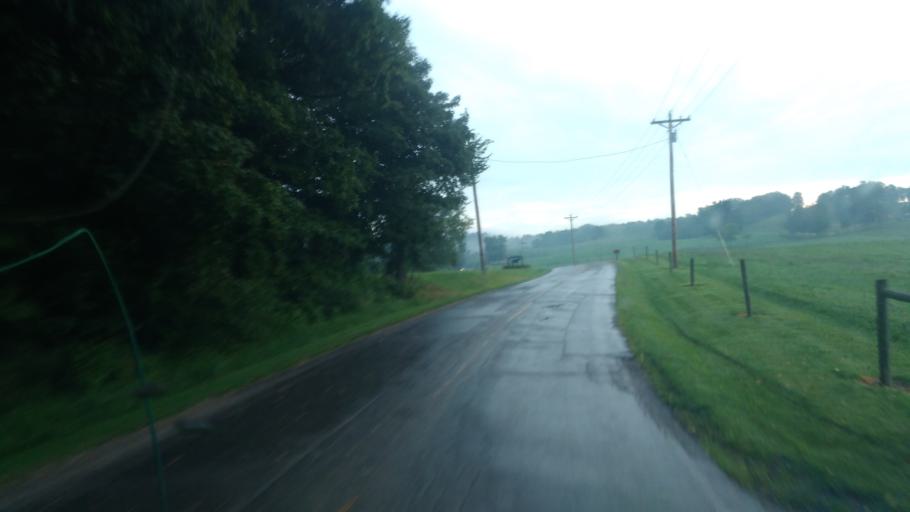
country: US
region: Ohio
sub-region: Guernsey County
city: Byesville
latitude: 39.9948
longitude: -81.3657
